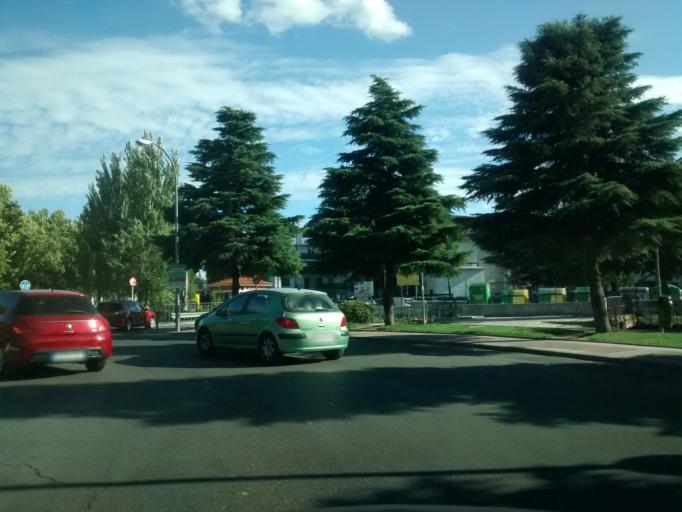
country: ES
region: Madrid
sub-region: Provincia de Madrid
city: Collado-Villalba
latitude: 40.6340
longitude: -4.0116
